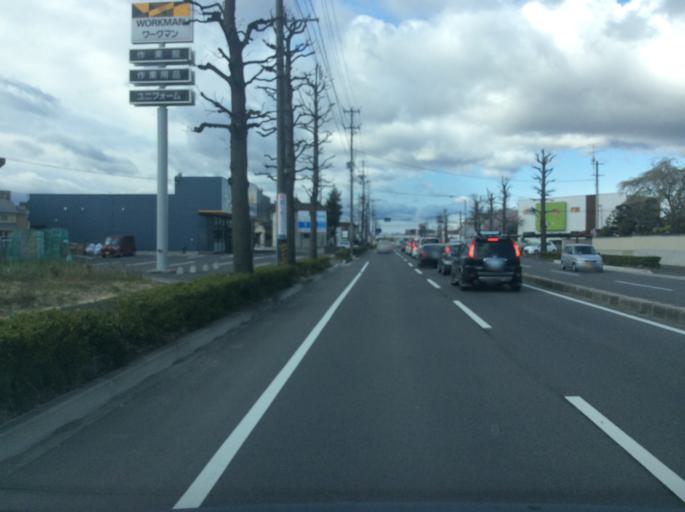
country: JP
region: Fukushima
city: Koriyama
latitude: 37.3827
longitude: 140.3901
